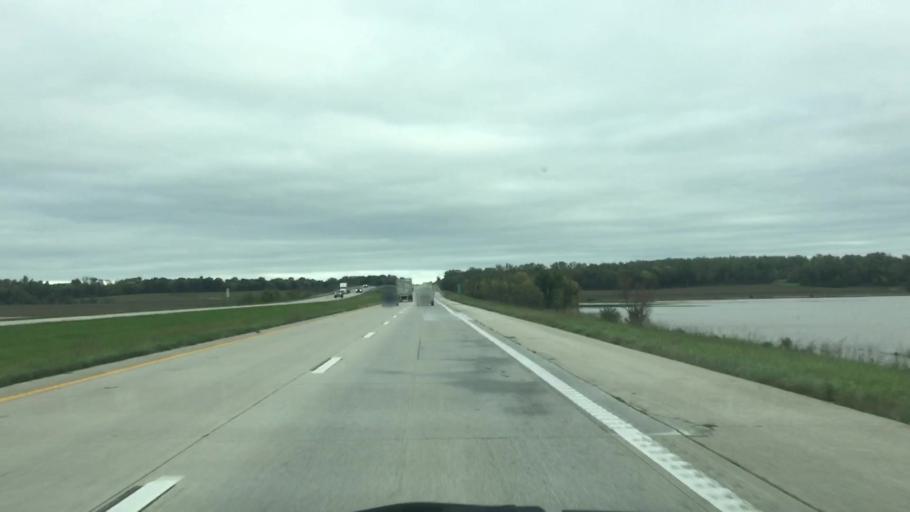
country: US
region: Missouri
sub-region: Daviess County
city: Gallatin
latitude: 40.0429
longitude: -94.0948
